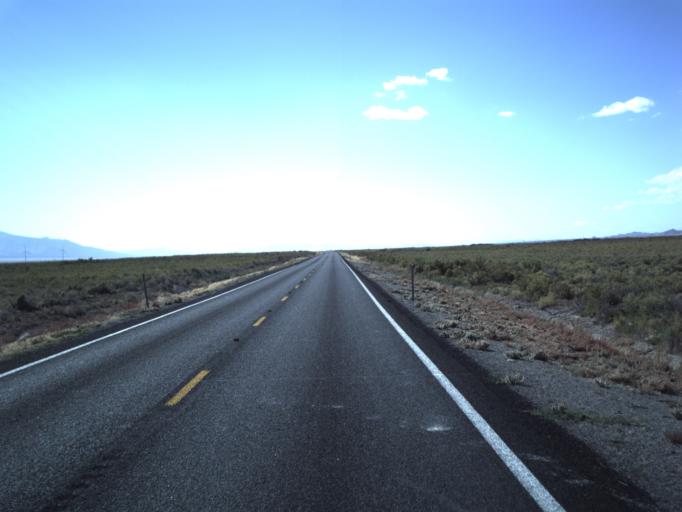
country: US
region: Utah
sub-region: Beaver County
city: Milford
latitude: 38.5630
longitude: -112.9907
